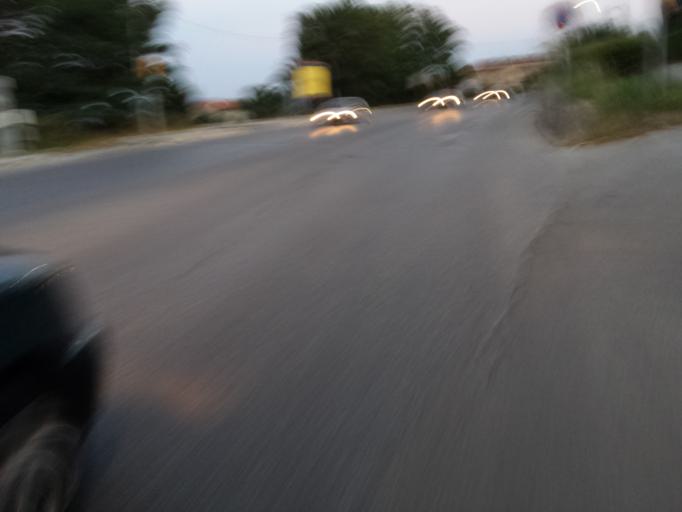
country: IT
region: Molise
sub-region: Provincia di Campobasso
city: Campobasso
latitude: 41.5807
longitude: 14.6752
